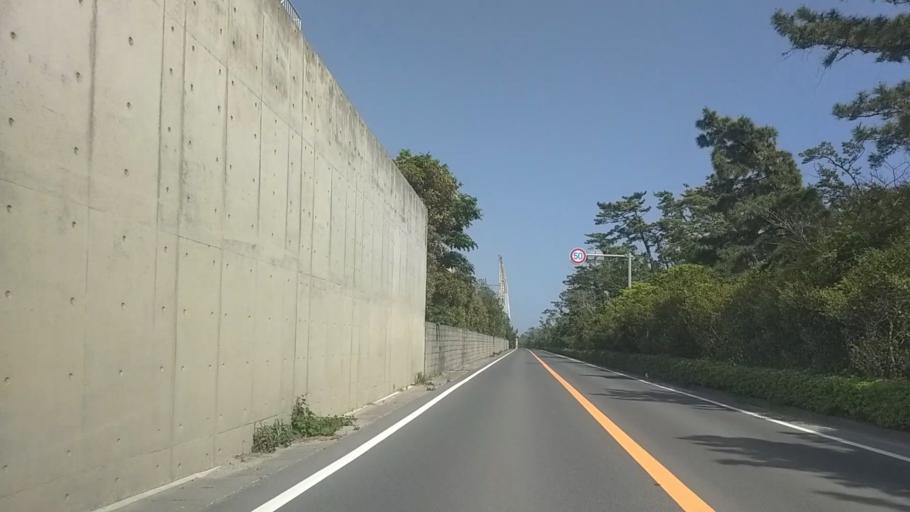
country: JP
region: Shizuoka
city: Hamamatsu
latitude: 34.6706
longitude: 137.6894
